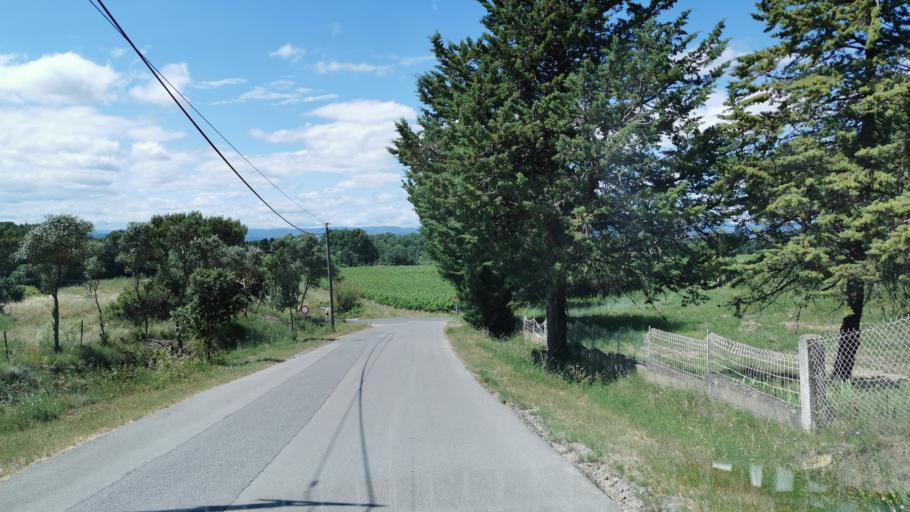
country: FR
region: Languedoc-Roussillon
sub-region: Departement de l'Aude
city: Marcorignan
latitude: 43.2345
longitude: 2.9316
